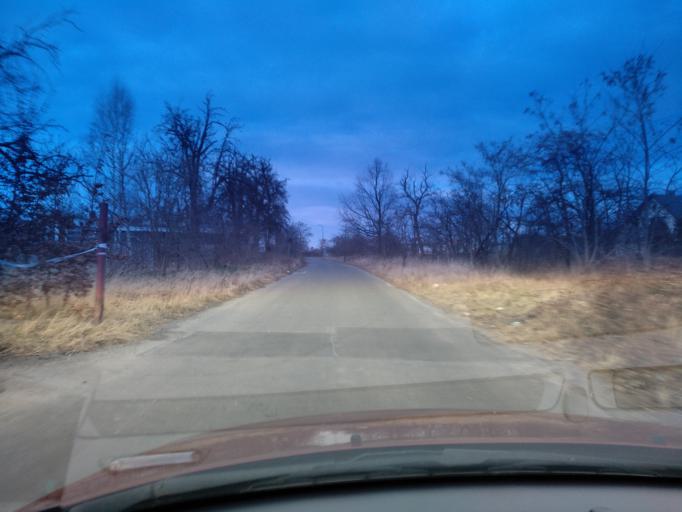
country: PL
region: Lower Silesian Voivodeship
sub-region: Powiat zgorzelecki
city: Zgorzelec
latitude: 51.1509
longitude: 15.0195
